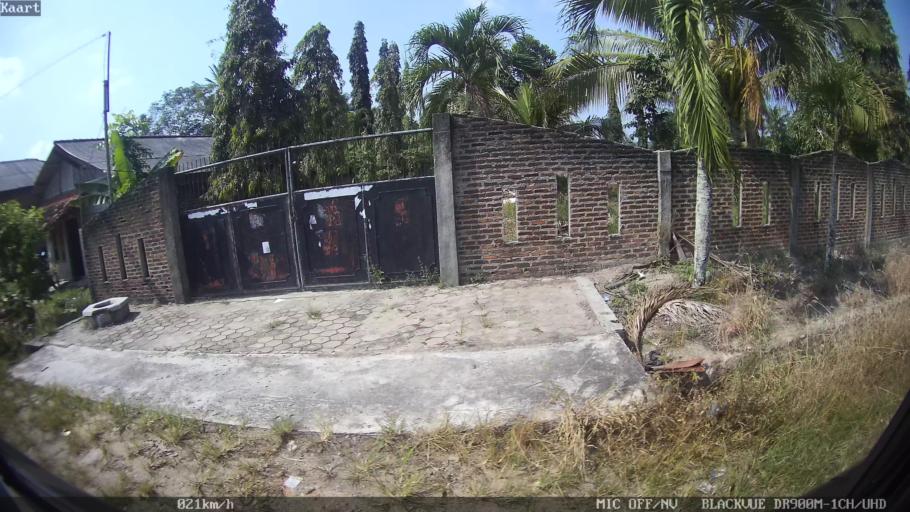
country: ID
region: Lampung
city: Natar
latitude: -5.2566
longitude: 105.2122
